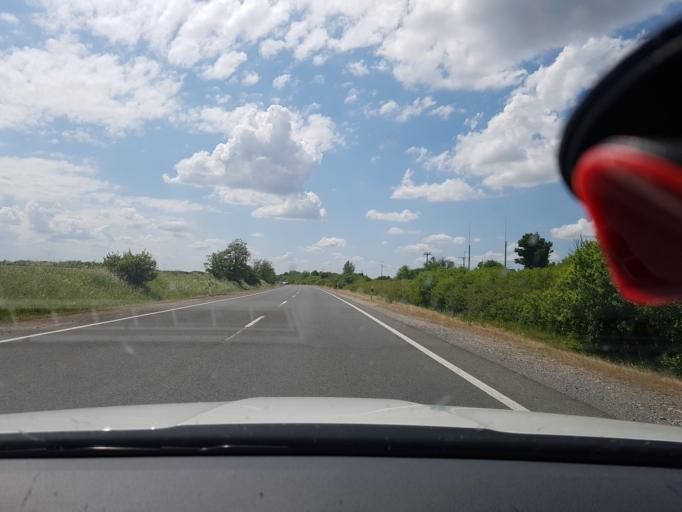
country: HU
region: Heves
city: Kompolt
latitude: 47.7519
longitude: 20.1643
